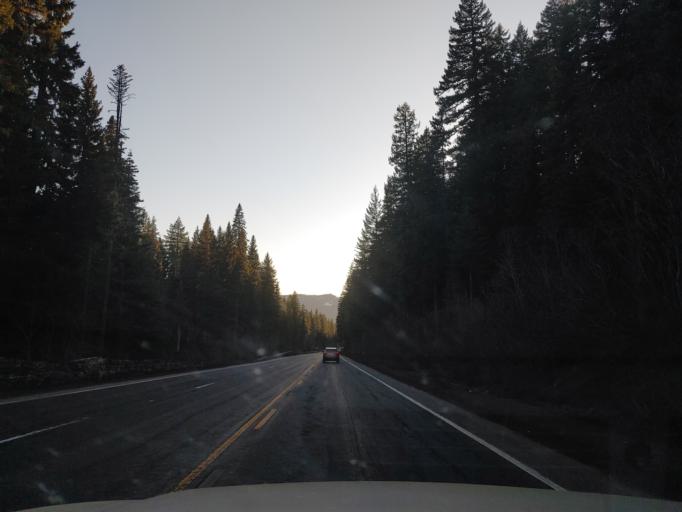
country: US
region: Oregon
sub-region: Lane County
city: Oakridge
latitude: 43.6200
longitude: -122.0733
